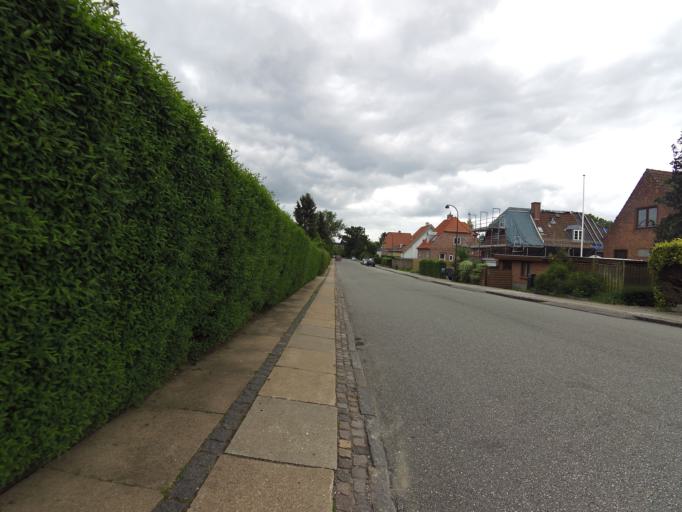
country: DK
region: Capital Region
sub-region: Frederiksberg Kommune
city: Frederiksberg
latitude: 55.7284
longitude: 12.5388
